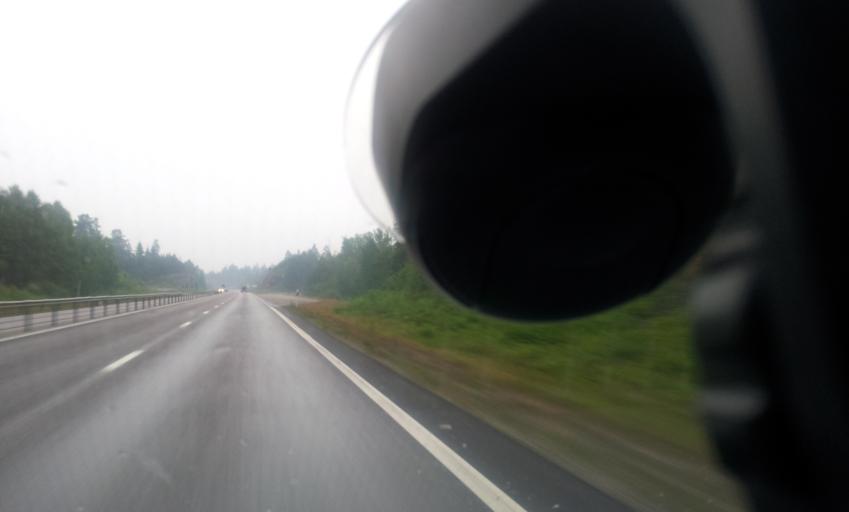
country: SE
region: Kalmar
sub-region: Vasterviks Kommun
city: Vaestervik
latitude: 57.7382
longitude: 16.5475
